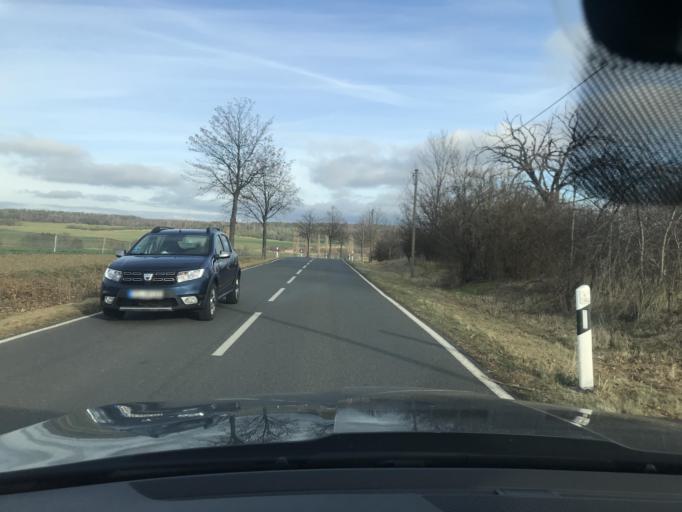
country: DE
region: Saxony-Anhalt
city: Weddersleben
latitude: 51.7693
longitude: 11.0982
